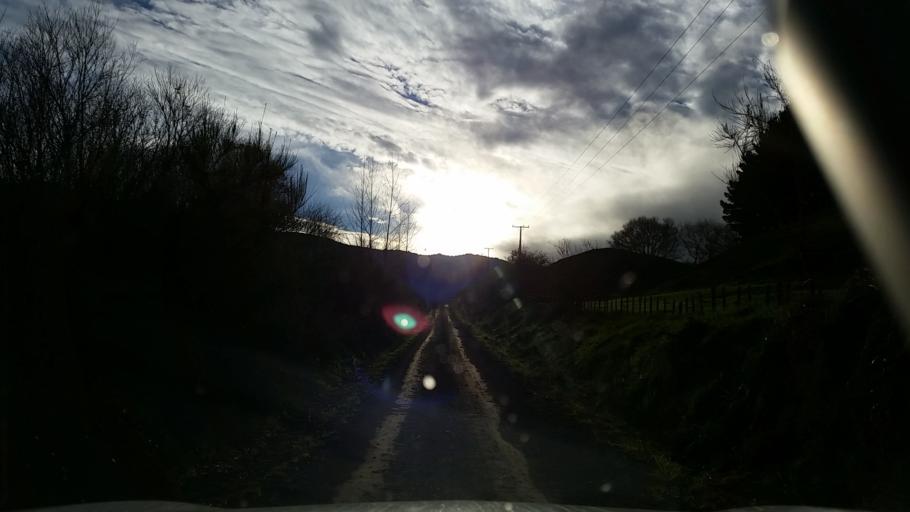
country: NZ
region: Bay of Plenty
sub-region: Rotorua District
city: Rotorua
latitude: -38.2996
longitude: 176.2751
